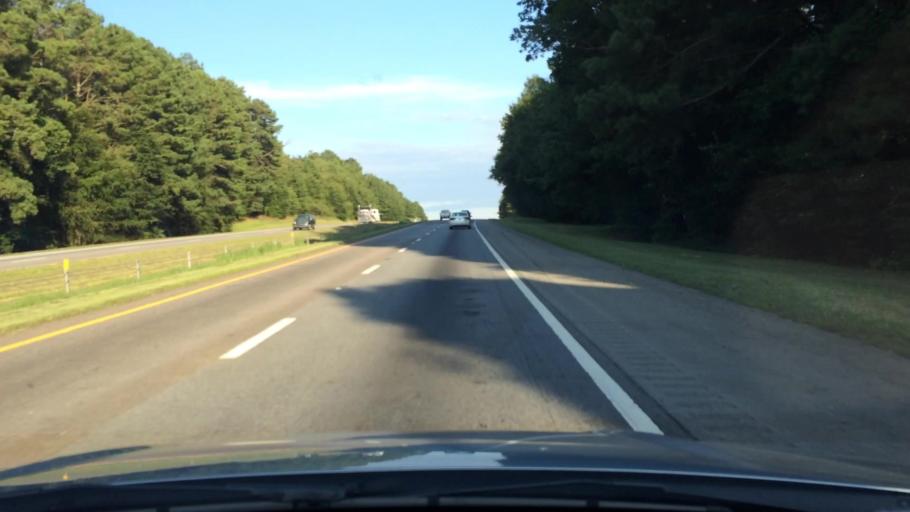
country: US
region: South Carolina
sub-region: Newberry County
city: Prosperity
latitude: 34.2810
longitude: -81.5256
